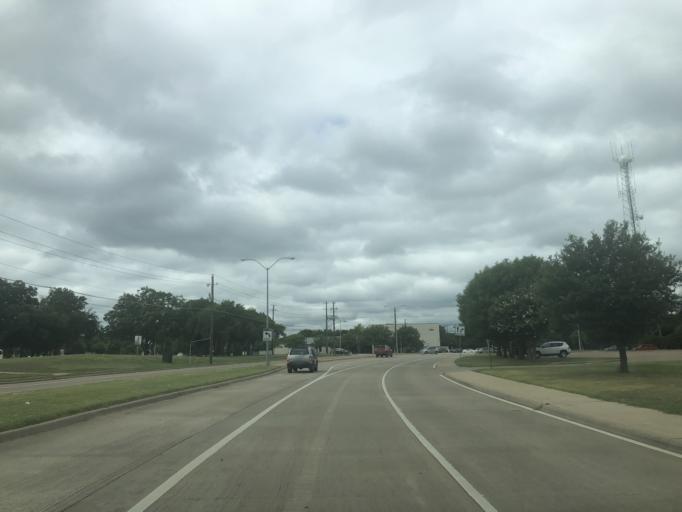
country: US
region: Texas
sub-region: Dallas County
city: Duncanville
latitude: 32.6426
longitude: -96.9538
